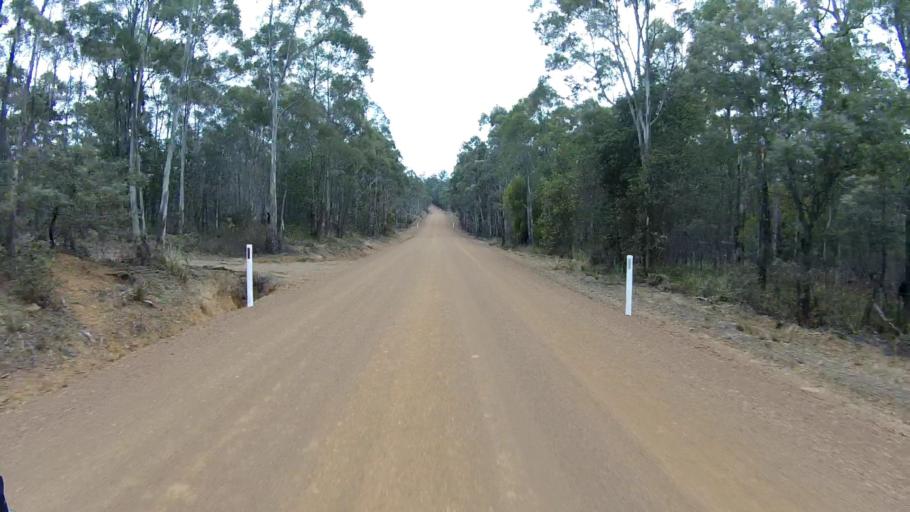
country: AU
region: Tasmania
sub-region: Sorell
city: Sorell
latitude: -42.5944
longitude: 147.8857
